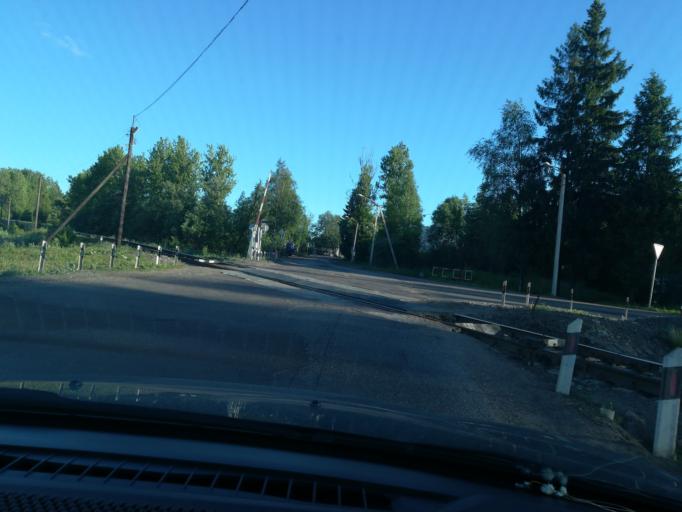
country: RU
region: Leningrad
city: Lesogorskiy
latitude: 61.0452
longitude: 28.9271
